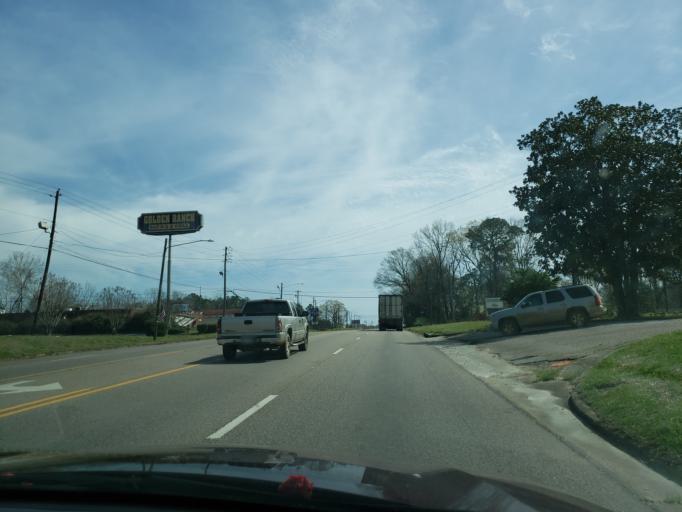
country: US
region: Alabama
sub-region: Dallas County
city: Selma
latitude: 32.4333
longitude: -87.0530
